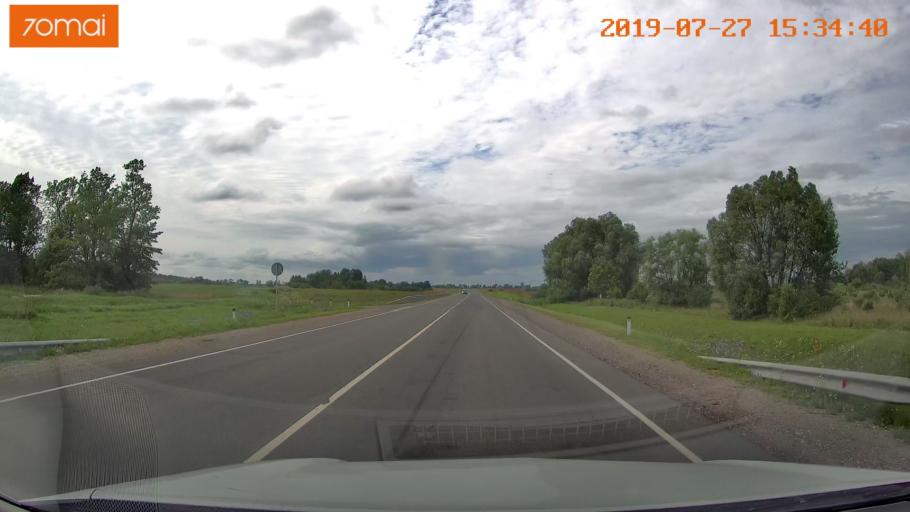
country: RU
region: Kaliningrad
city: Nesterov
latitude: 54.6122
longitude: 22.4177
